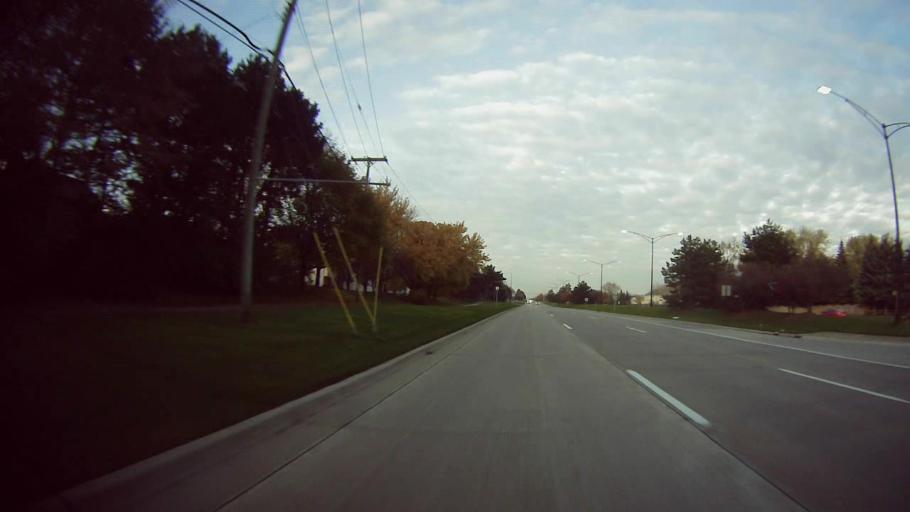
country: US
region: Michigan
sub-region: Oakland County
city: Clawson
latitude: 42.5637
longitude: -83.0955
